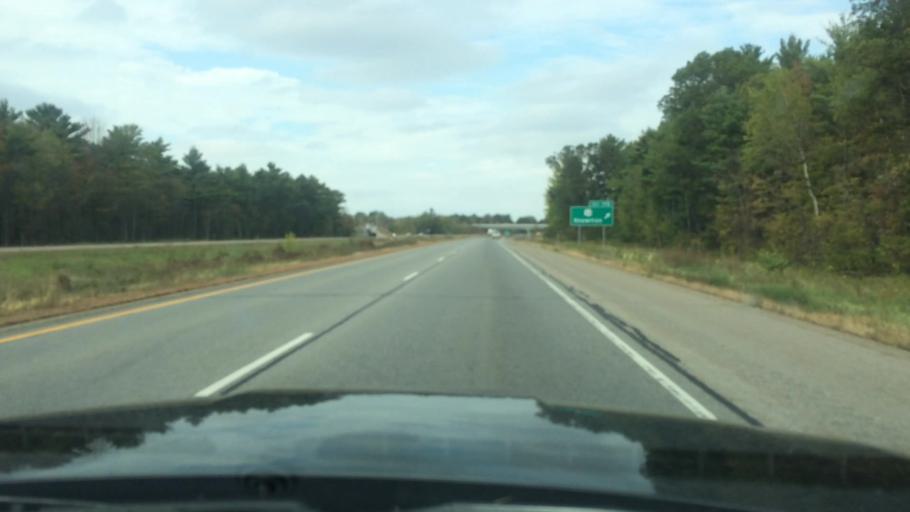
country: US
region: Wisconsin
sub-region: Marathon County
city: Mosinee
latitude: 44.7245
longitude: -89.6729
